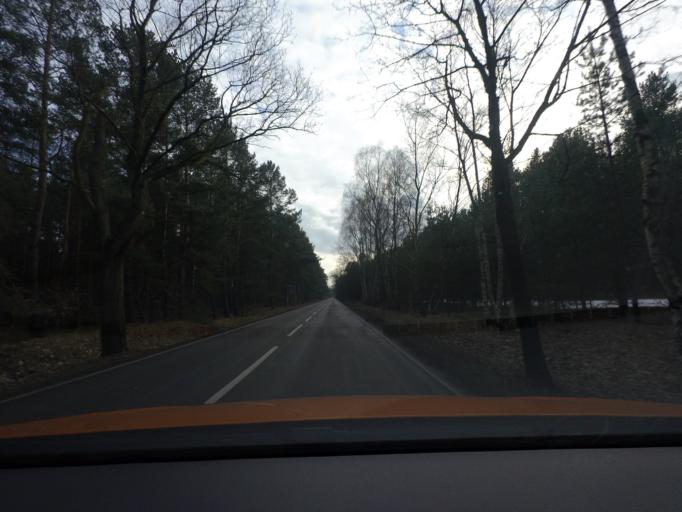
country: DE
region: Brandenburg
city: Birkenwerder
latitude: 52.7186
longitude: 13.3671
